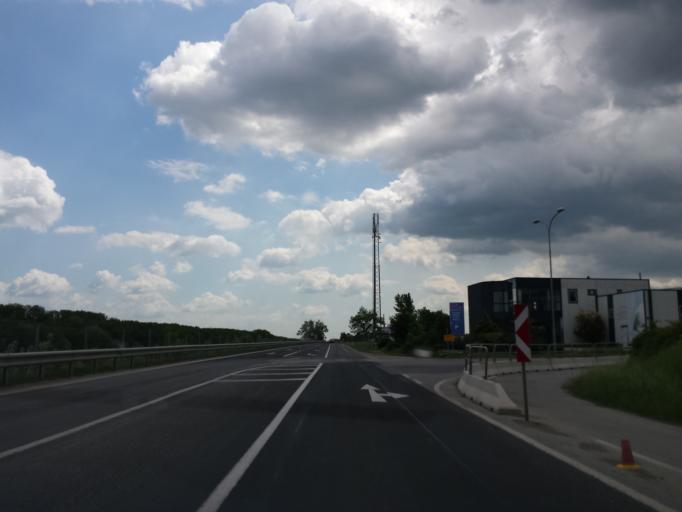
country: AT
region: Lower Austria
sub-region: Politischer Bezirk Wien-Umgebung
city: Fischamend Dorf
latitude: 48.1263
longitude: 16.5899
